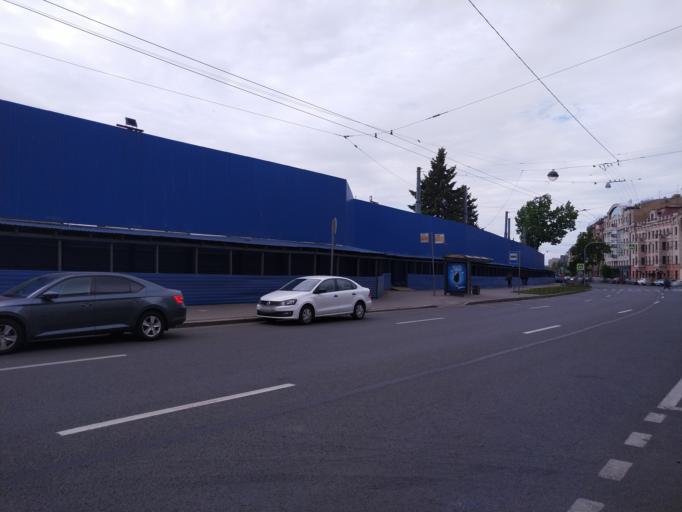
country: RU
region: St.-Petersburg
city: Saint Petersburg
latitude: 59.9487
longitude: 30.3027
